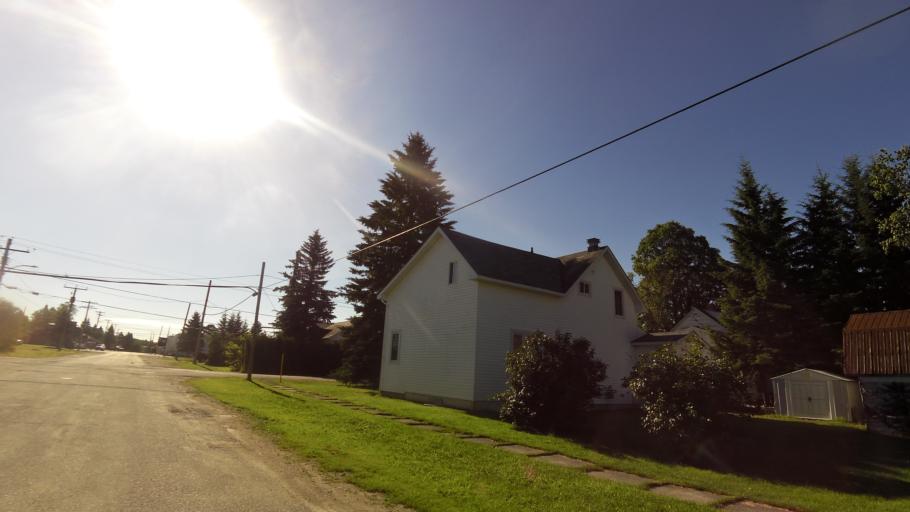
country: CA
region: Ontario
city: Iroquois Falls
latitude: 48.5361
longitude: -80.4689
